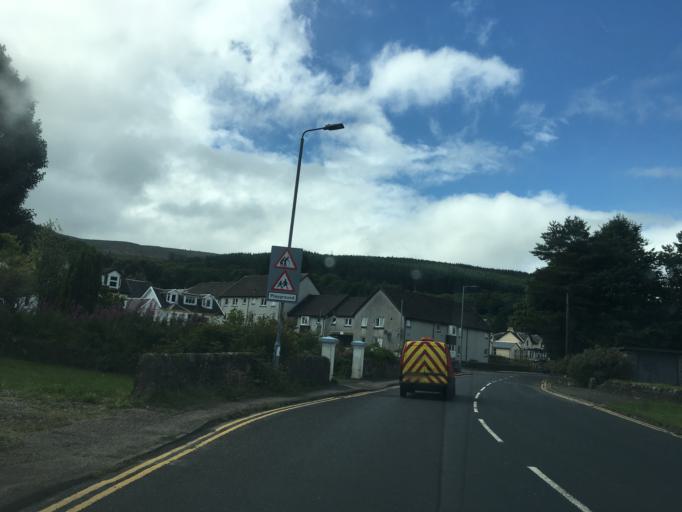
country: GB
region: Scotland
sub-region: Argyll and Bute
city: Dunoon
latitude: 55.9805
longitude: -4.9431
